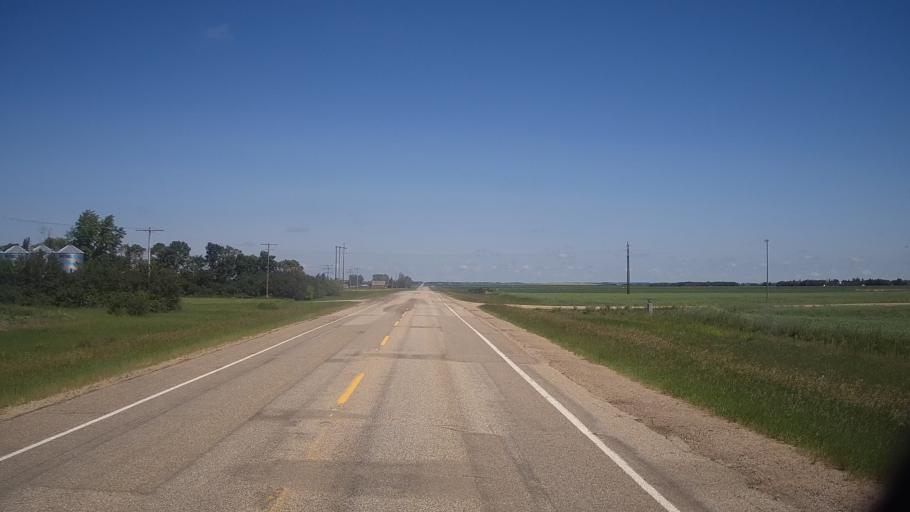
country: CA
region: Saskatchewan
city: Saskatoon
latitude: 51.9806
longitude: -106.0754
